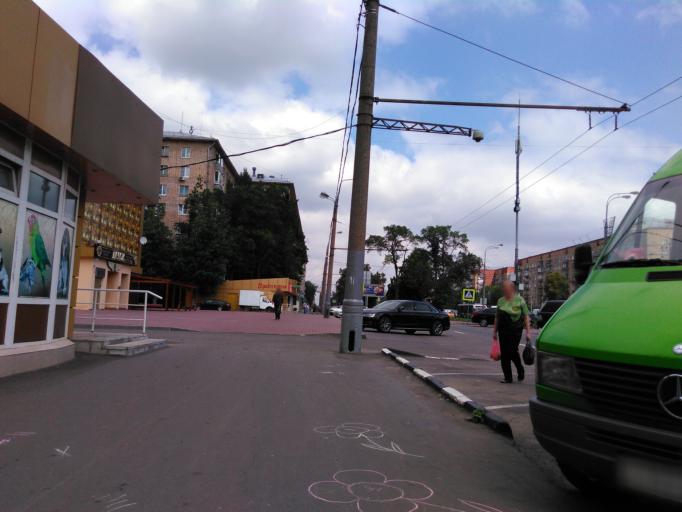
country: RU
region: Moskovskaya
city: Semenovskoye
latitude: 55.6756
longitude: 37.5261
